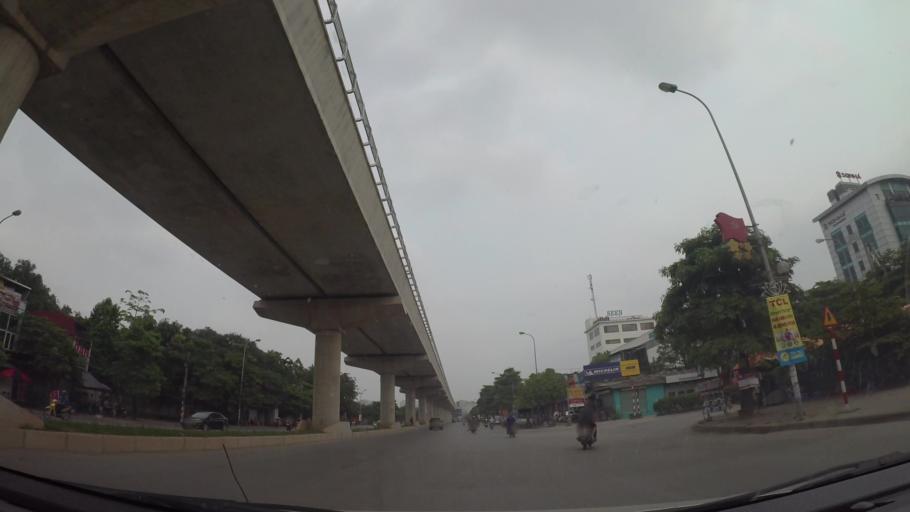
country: VN
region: Ha Noi
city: Cau Dien
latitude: 21.0496
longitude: 105.7405
